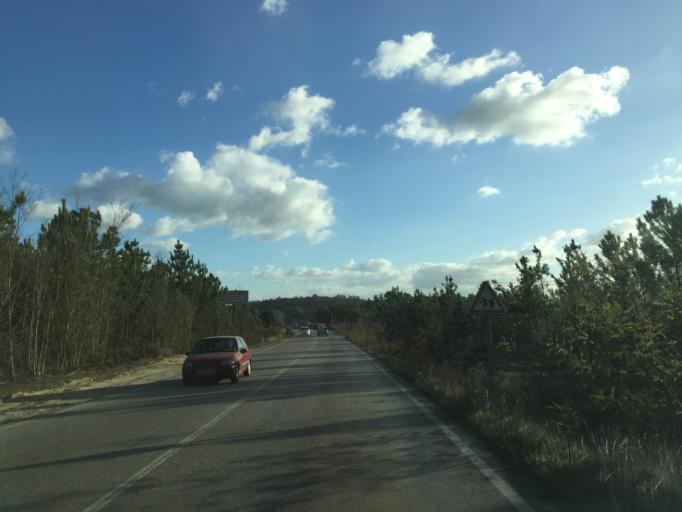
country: PT
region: Leiria
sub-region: Leiria
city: Monte Redondo
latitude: 39.8716
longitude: -8.8391
